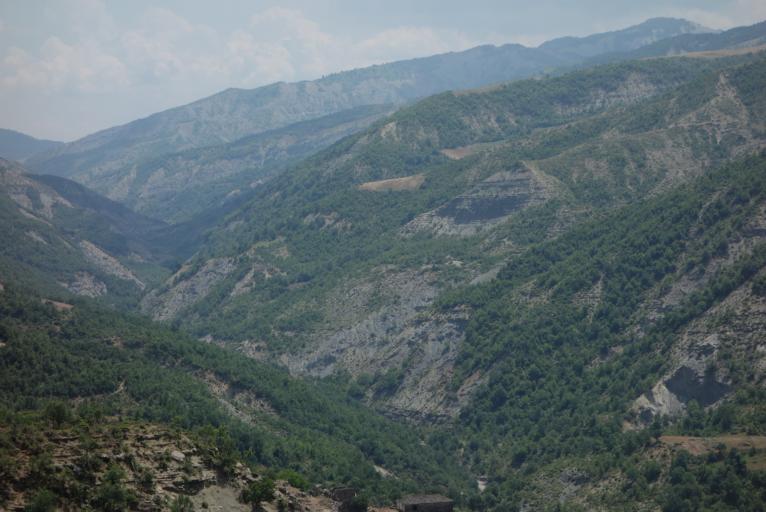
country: AL
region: Berat
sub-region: Rrethi i Skraparit
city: Cepan
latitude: 40.4005
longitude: 20.3403
